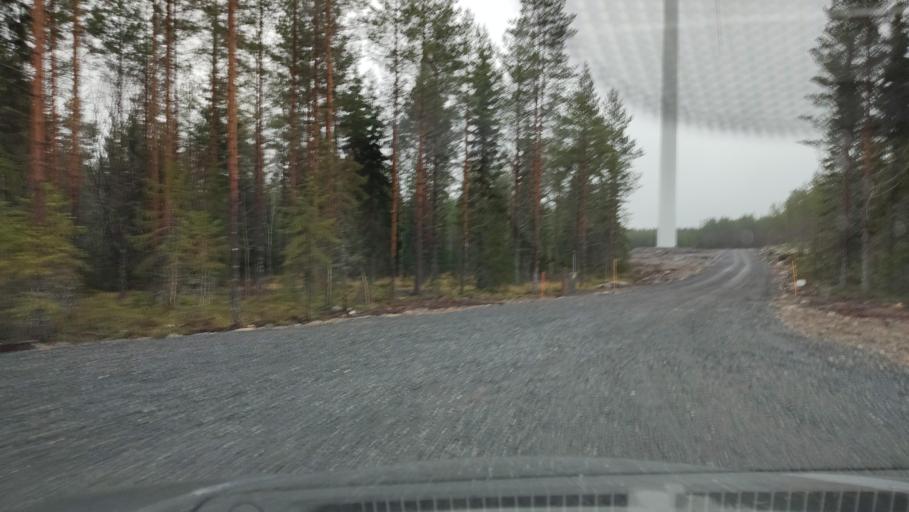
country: FI
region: Southern Ostrobothnia
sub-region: Suupohja
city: Karijoki
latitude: 62.1582
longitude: 21.6130
